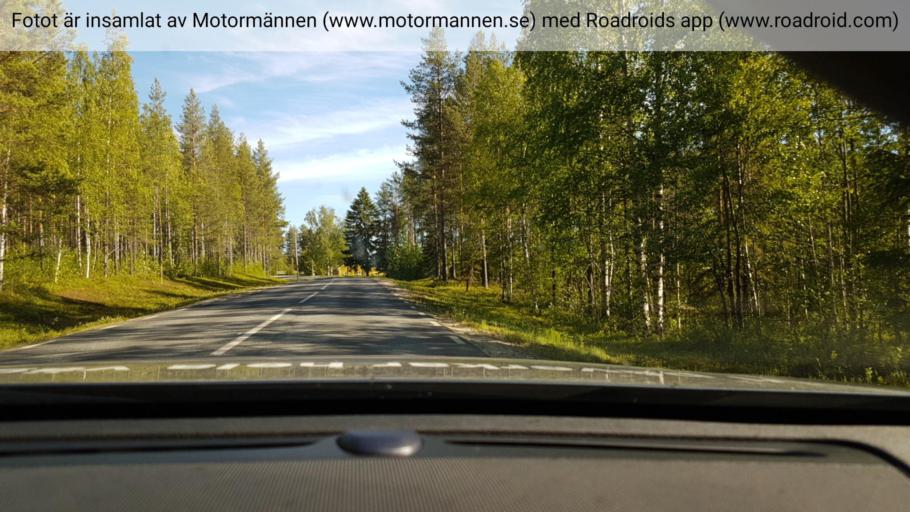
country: SE
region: Vaesterbotten
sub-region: Norsjo Kommun
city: Norsjoe
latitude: 64.7187
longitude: 19.1356
